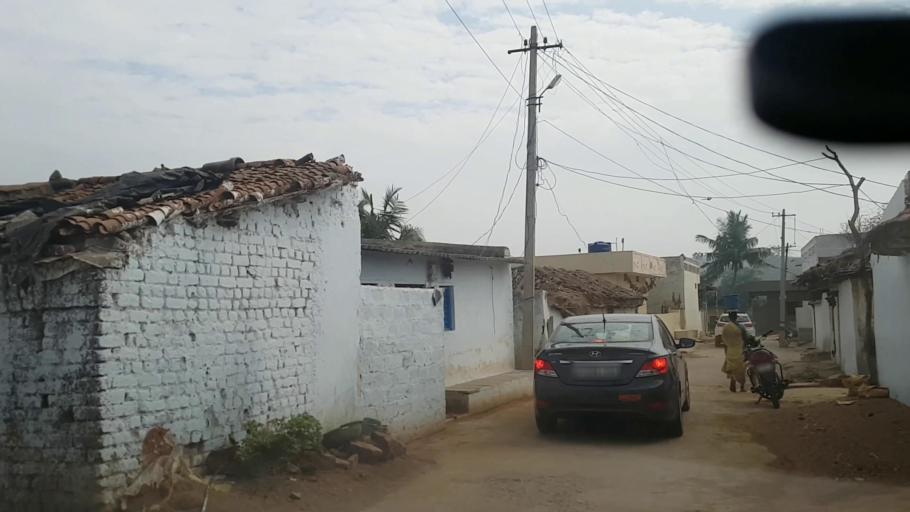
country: IN
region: Telangana
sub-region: Rangareddi
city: Lal Bahadur Nagar
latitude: 17.1729
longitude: 78.7790
